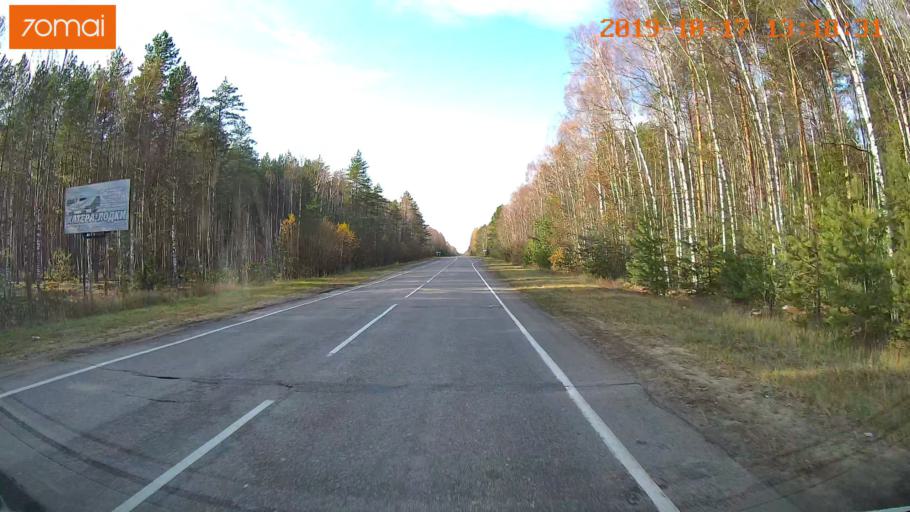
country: RU
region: Rjazan
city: Gus'-Zheleznyy
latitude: 55.0634
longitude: 41.0961
